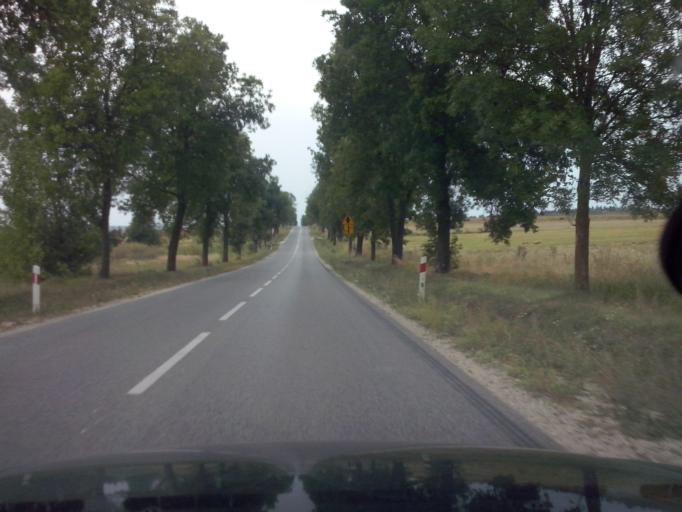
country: PL
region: Swietokrzyskie
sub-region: Powiat kielecki
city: Morawica
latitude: 50.7297
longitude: 20.6114
